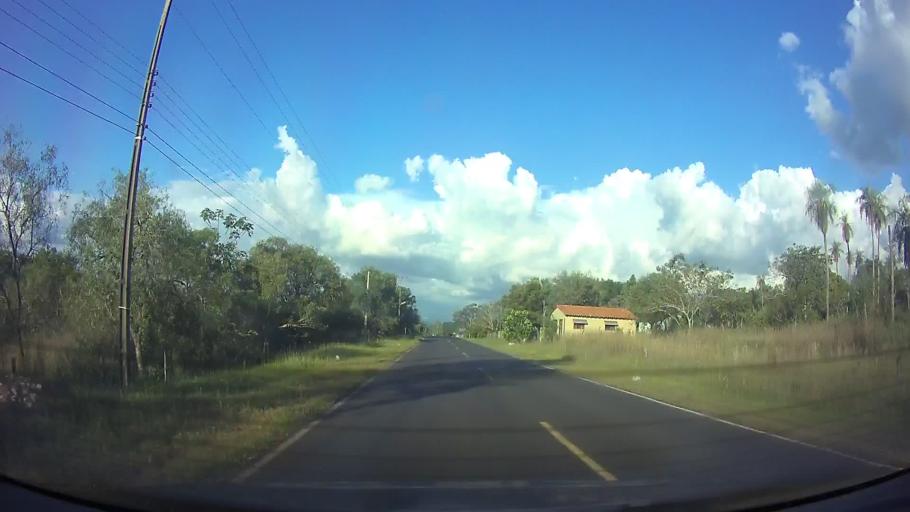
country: PY
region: Cordillera
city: Emboscada
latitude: -25.1703
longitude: -57.2775
